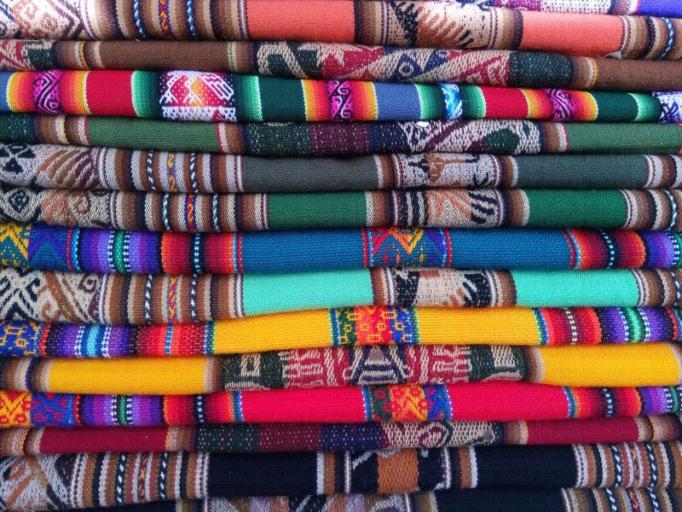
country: PE
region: Cusco
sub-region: Provincia de Calca
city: Pisac
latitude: -13.4209
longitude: -71.8504
